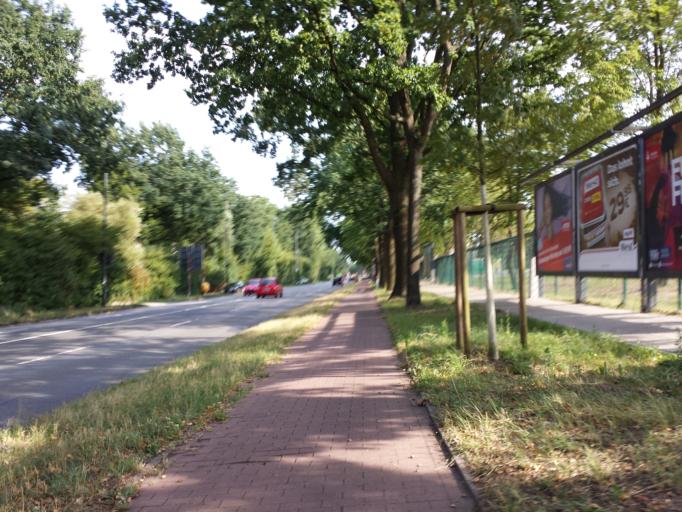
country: DE
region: Bremen
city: Bremen
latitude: 53.0613
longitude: 8.7899
